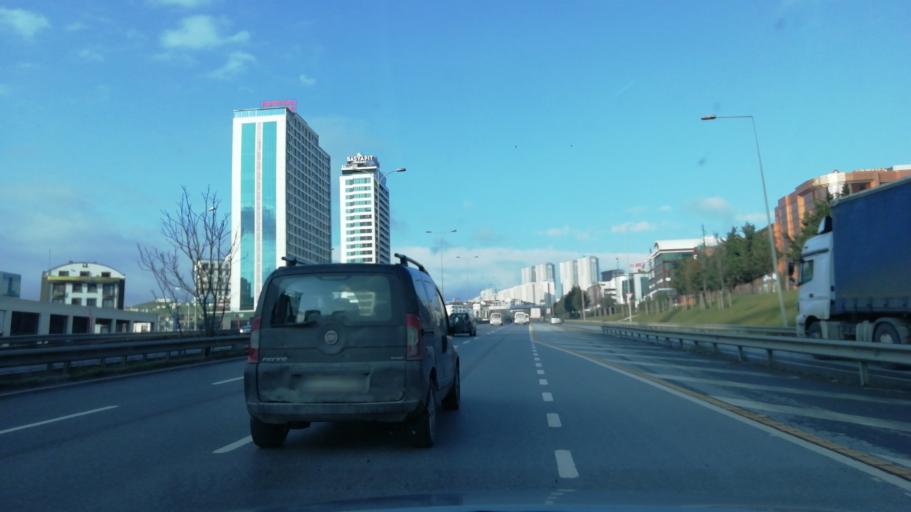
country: TR
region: Istanbul
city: Esenyurt
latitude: 41.0211
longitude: 28.6807
